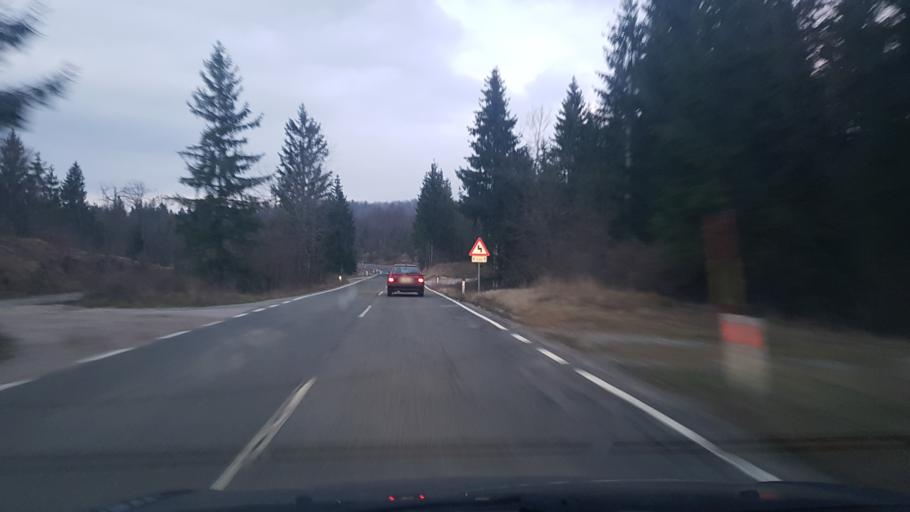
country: SI
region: Idrija
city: Idrija
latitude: 45.9341
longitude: 14.0670
